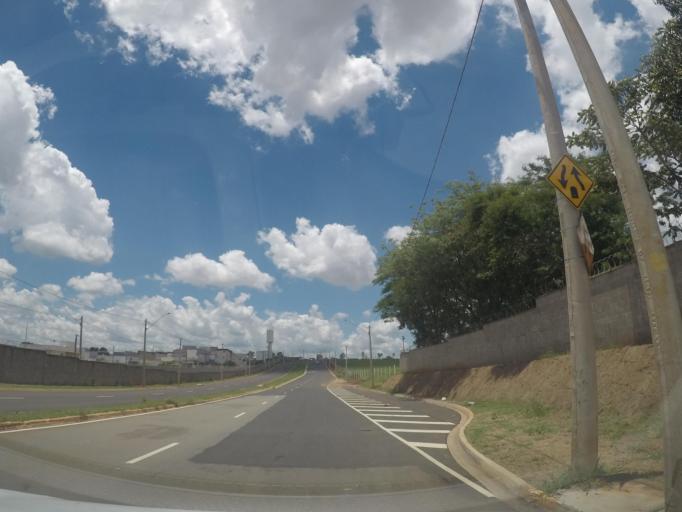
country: BR
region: Sao Paulo
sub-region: Hortolandia
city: Hortolandia
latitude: -22.8322
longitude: -47.2181
